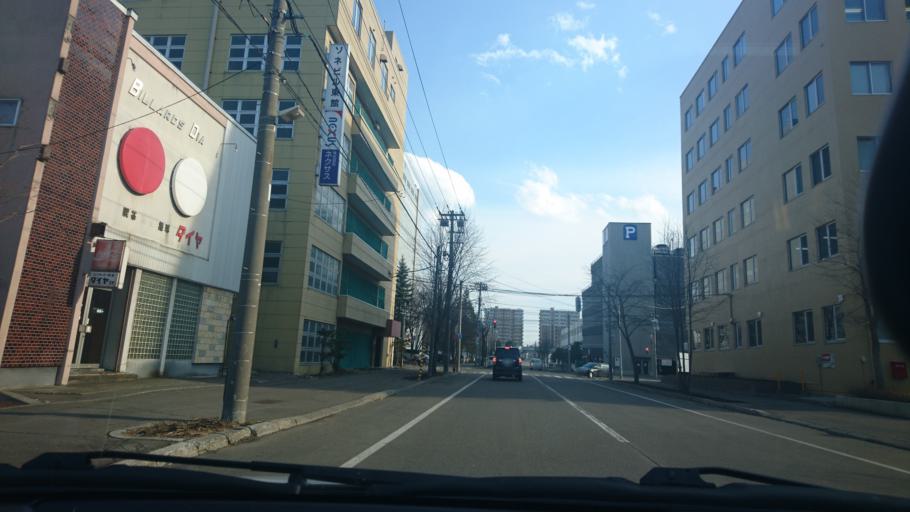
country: JP
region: Hokkaido
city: Obihiro
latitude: 42.9250
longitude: 143.1954
